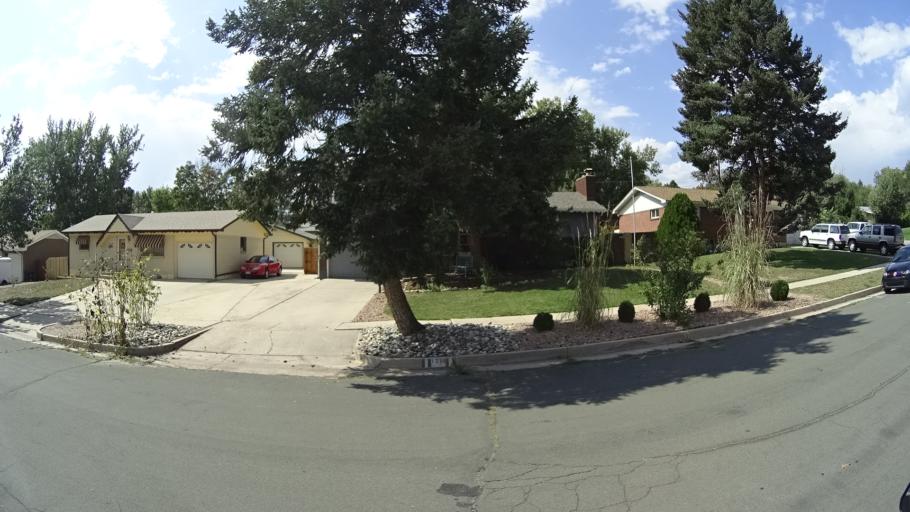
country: US
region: Colorado
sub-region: El Paso County
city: Colorado Springs
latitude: 38.8502
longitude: -104.7686
